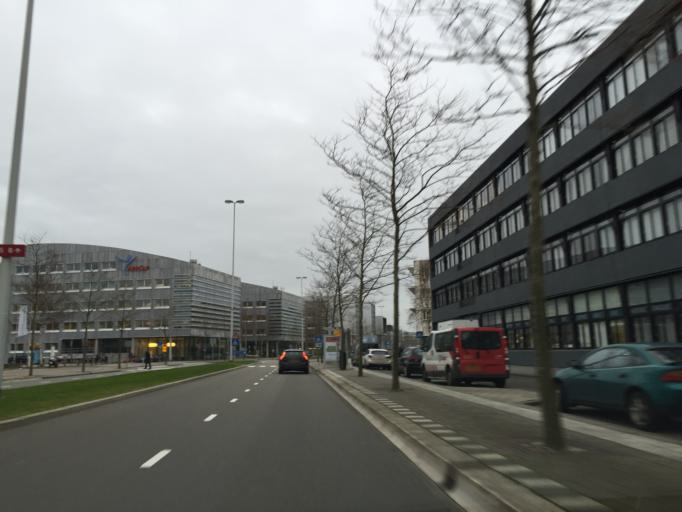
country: NL
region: North Holland
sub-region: Gemeente Amstelveen
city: Amstelveen
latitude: 52.3111
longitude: 4.8127
